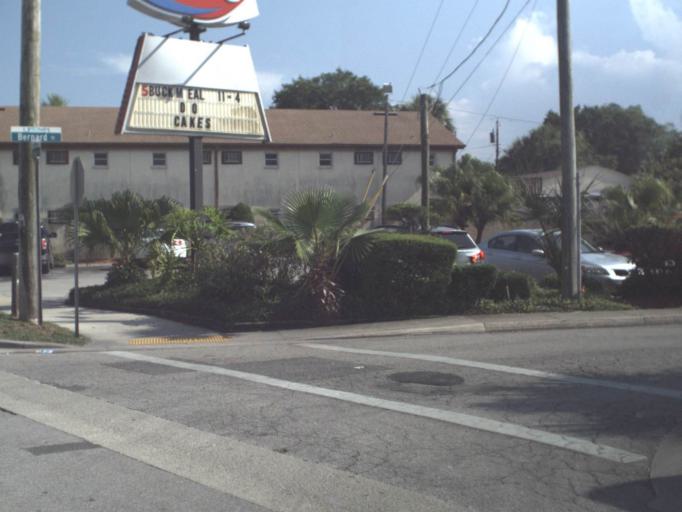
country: US
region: Florida
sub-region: Saint Johns County
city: Saint Augustine
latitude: 29.9034
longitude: -81.3169
